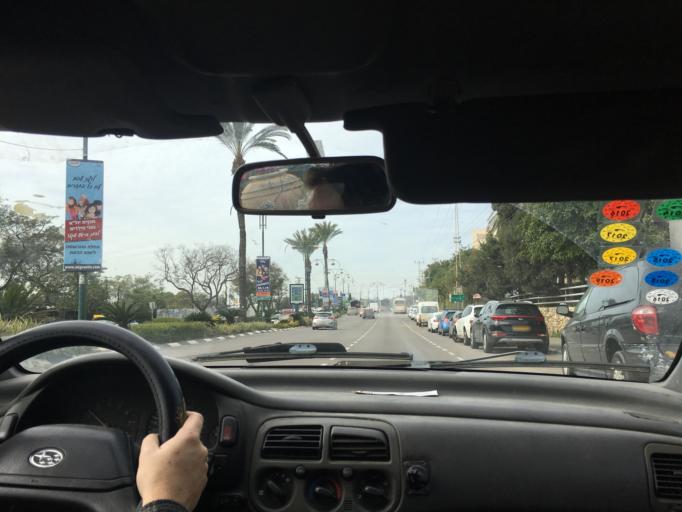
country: IL
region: Tel Aviv
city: Ramat HaSharon
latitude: 32.1378
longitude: 34.8372
